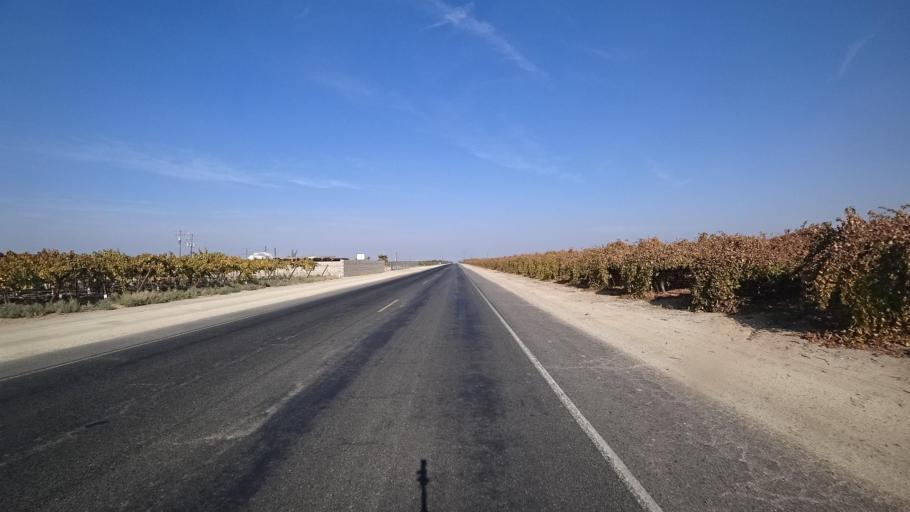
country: US
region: California
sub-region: Kern County
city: McFarland
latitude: 35.6861
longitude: -119.1793
